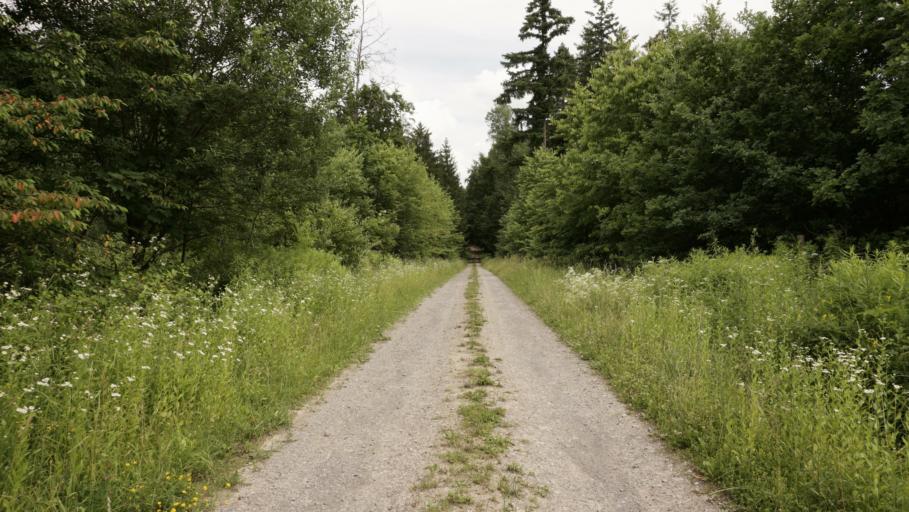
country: DE
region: Baden-Wuerttemberg
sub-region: Karlsruhe Region
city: Mosbach
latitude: 49.3285
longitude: 9.1802
